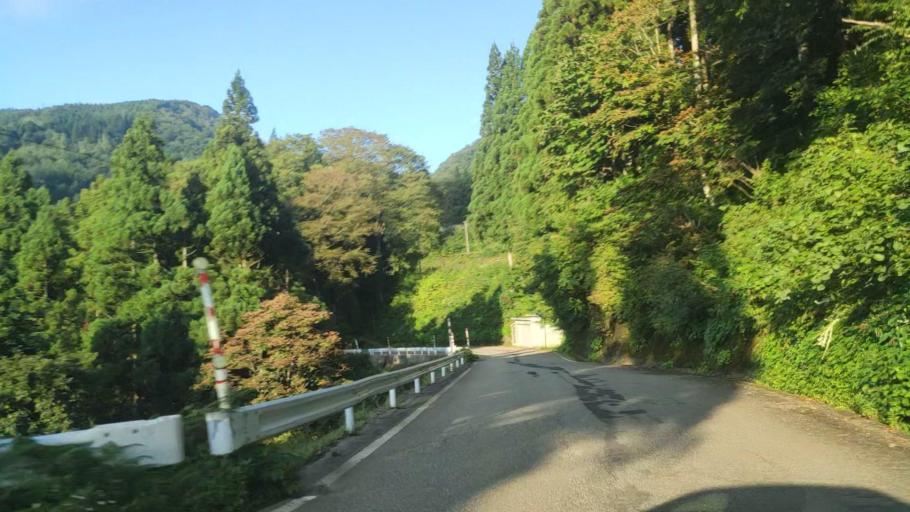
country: JP
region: Toyama
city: Yatsuomachi-higashikumisaka
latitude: 36.4766
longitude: 137.0311
